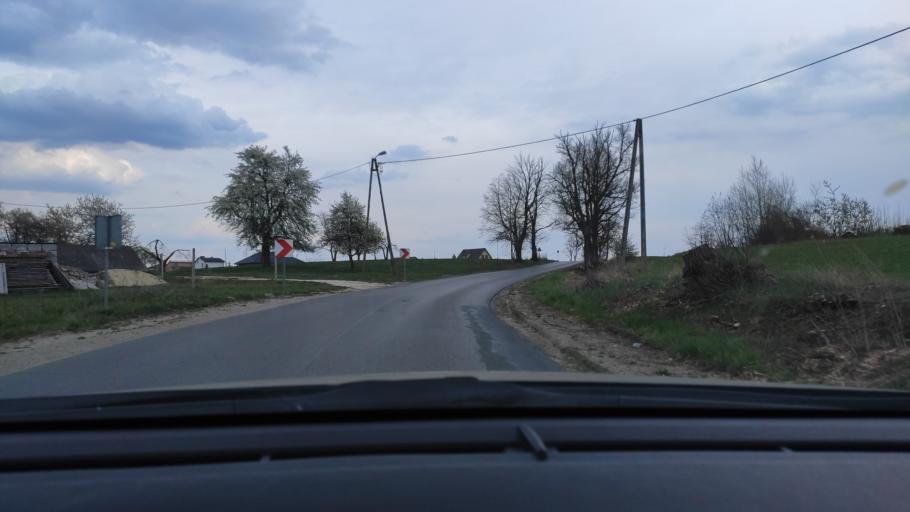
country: PL
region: Masovian Voivodeship
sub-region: Powiat kozienicki
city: Ryczywol
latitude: 51.5946
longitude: 21.3508
